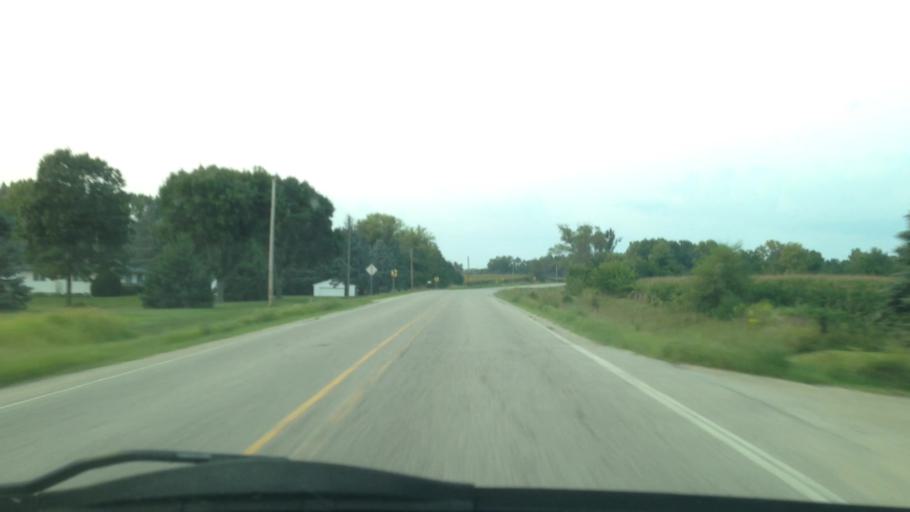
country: US
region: Iowa
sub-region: Benton County
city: Urbana
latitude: 42.1548
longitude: -91.8777
